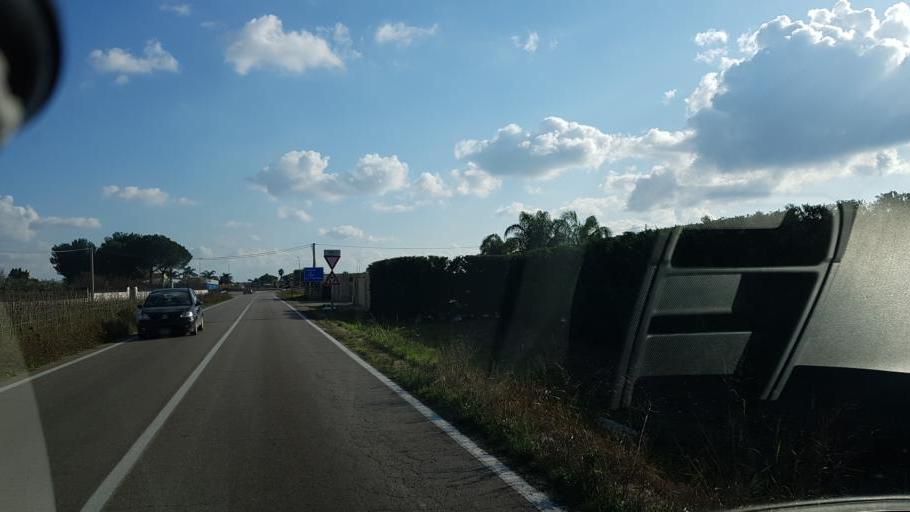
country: IT
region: Apulia
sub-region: Provincia di Lecce
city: Leverano
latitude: 40.3074
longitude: 17.9882
